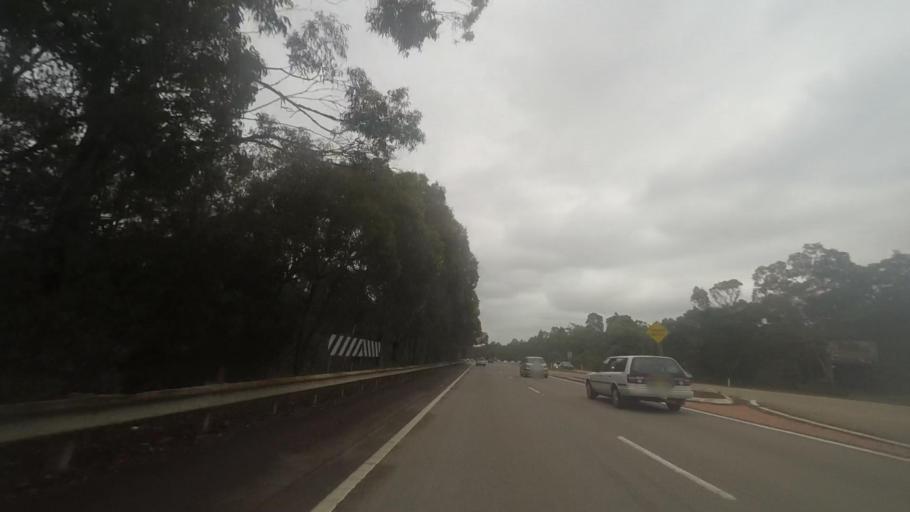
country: AU
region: New South Wales
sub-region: Port Stephens Shire
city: Raymond Terrace
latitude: -32.7012
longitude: 151.8028
